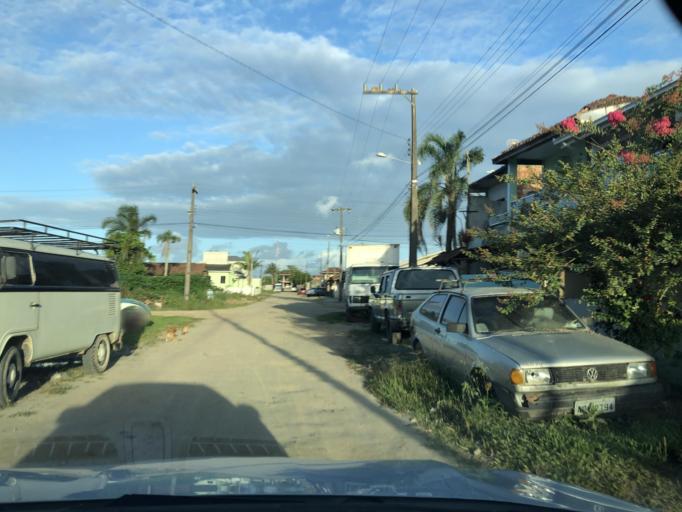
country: BR
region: Santa Catarina
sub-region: Sao Francisco Do Sul
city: Sao Francisco do Sul
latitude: -26.2353
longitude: -48.5206
